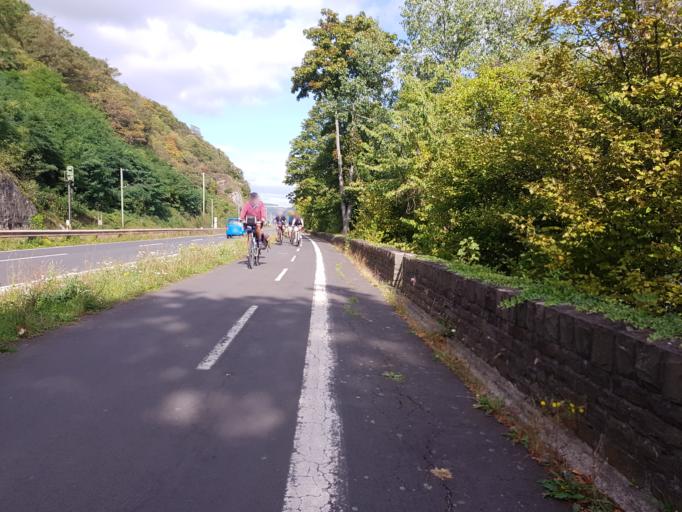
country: DE
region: Rheinland-Pfalz
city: Kaub
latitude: 50.0763
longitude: 7.7697
